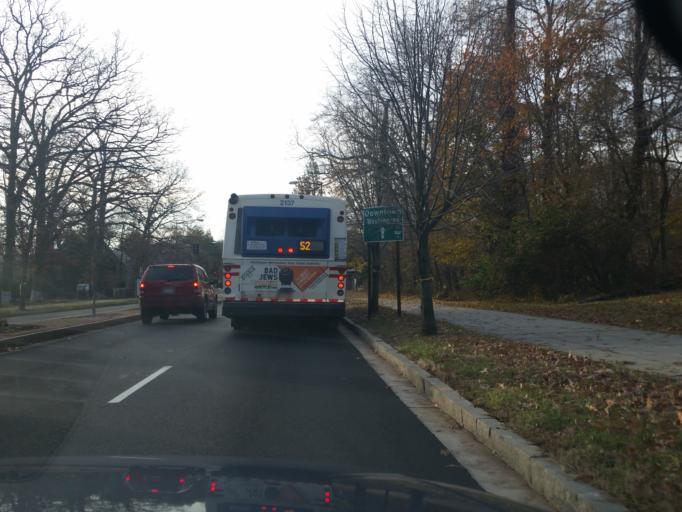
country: US
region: Maryland
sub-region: Montgomery County
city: Takoma Park
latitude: 38.9537
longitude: -77.0365
